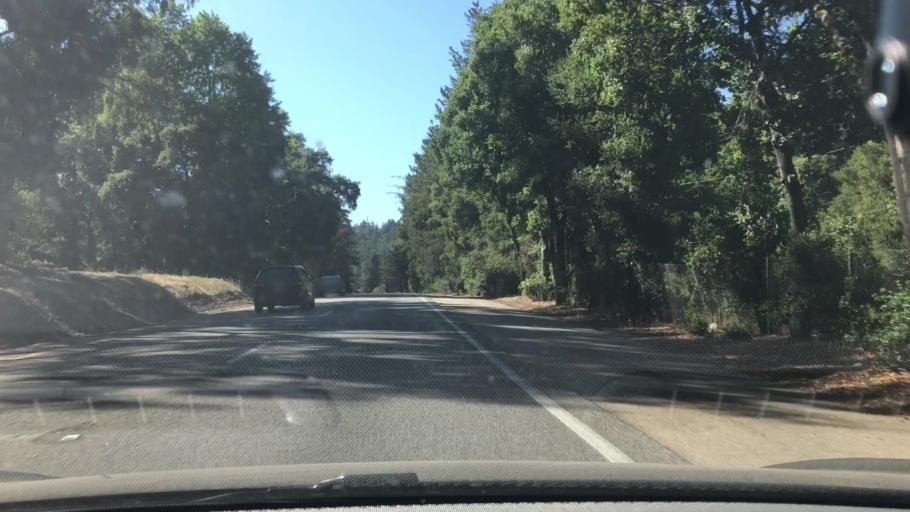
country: US
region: California
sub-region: Santa Cruz County
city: Pasatiempo
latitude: 37.0143
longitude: -122.0247
